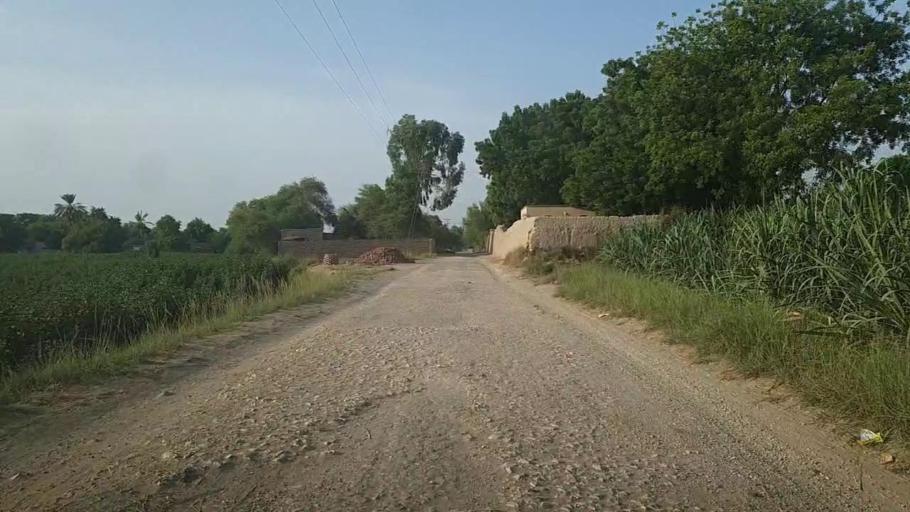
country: PK
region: Sindh
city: Ubauro
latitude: 28.3262
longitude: 69.7968
